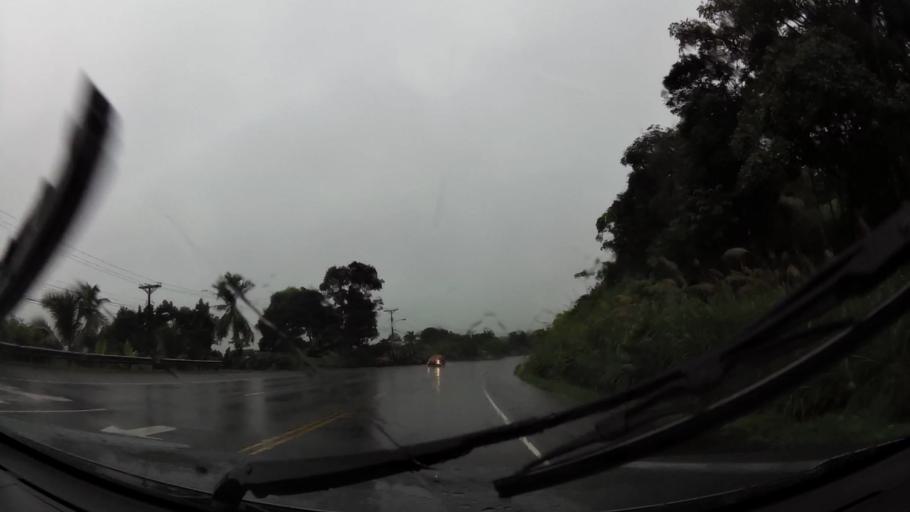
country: PA
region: Colon
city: Rio Rita
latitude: 9.3123
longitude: -79.7935
